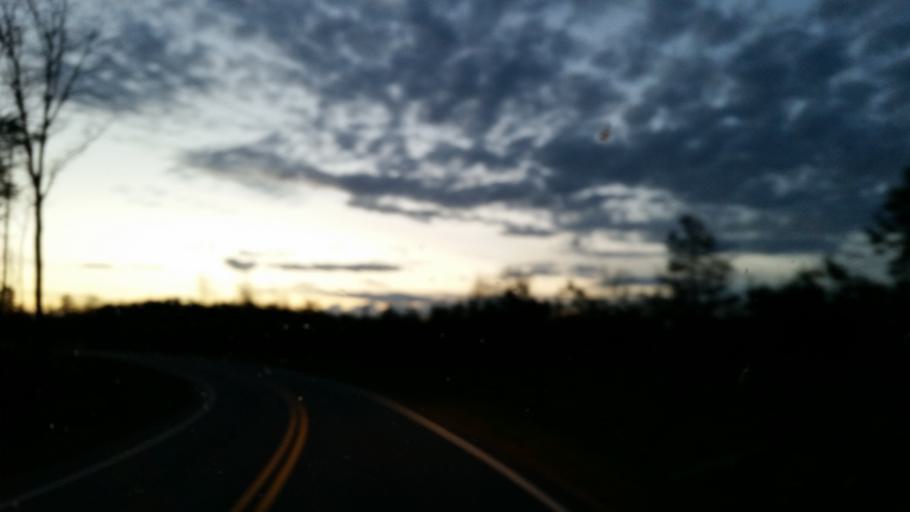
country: US
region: Georgia
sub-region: Cherokee County
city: Ball Ground
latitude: 34.3100
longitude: -84.4305
